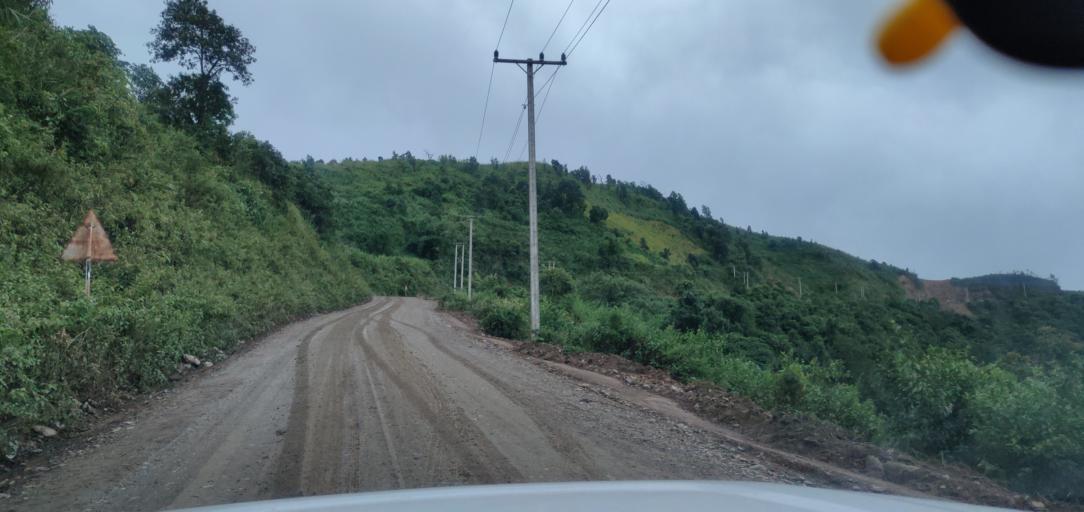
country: LA
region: Phongsali
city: Phongsali
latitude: 21.4275
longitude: 102.1682
